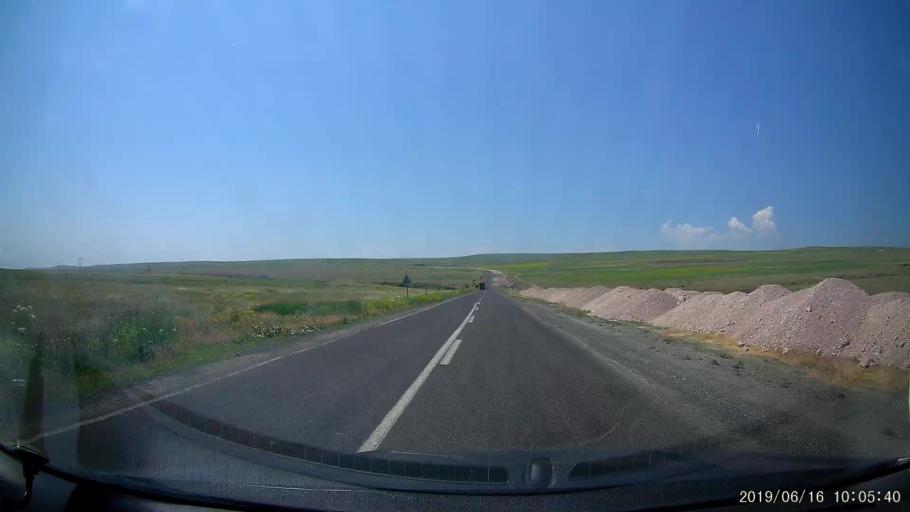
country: TR
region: Kars
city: Digor
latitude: 40.2667
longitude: 43.5393
